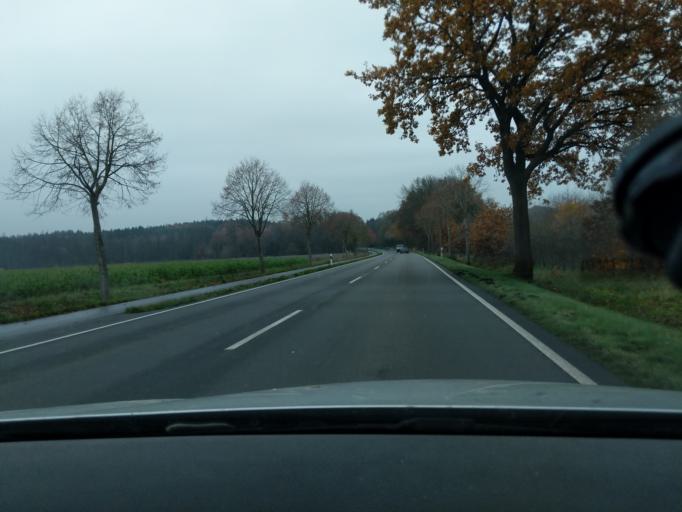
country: DE
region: Lower Saxony
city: Zeven
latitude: 53.2541
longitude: 9.2761
